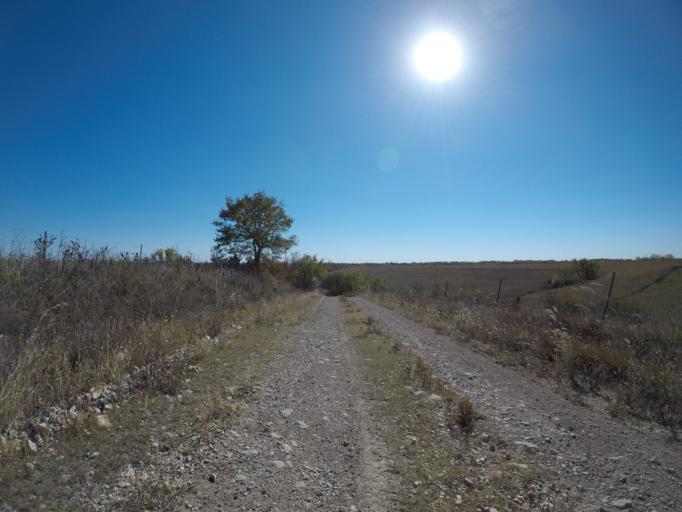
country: US
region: Kansas
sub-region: Wabaunsee County
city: Alma
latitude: 38.9861
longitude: -96.4642
